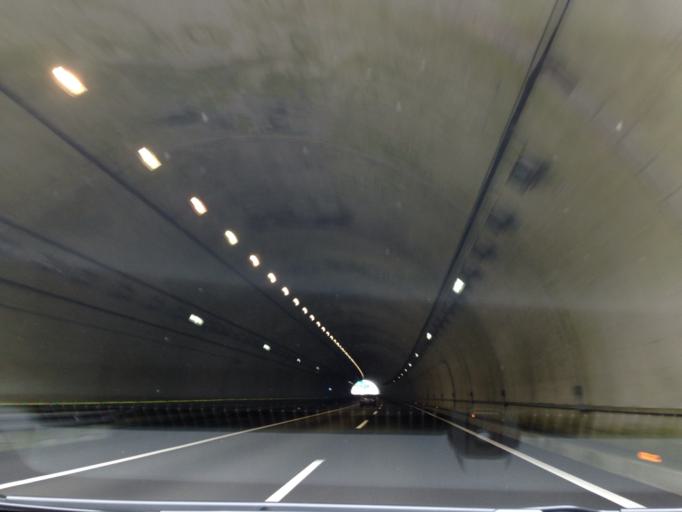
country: JP
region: Shizuoka
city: Fujinomiya
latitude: 35.1125
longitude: 138.4861
